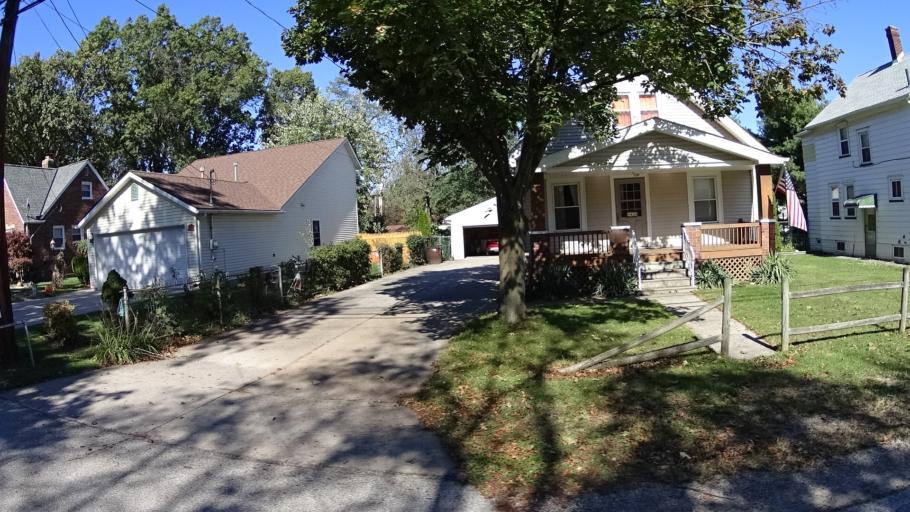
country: US
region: Ohio
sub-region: Lorain County
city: Lorain
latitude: 41.4280
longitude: -82.1598
